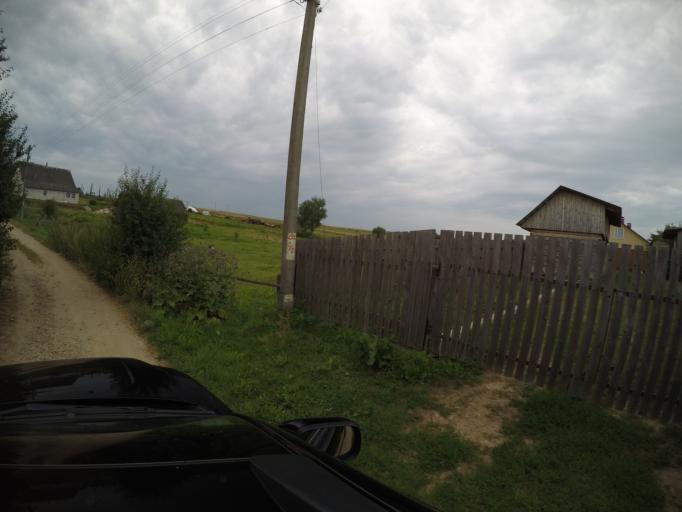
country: BY
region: Grodnenskaya
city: Hal'shany
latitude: 54.2597
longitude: 26.0099
